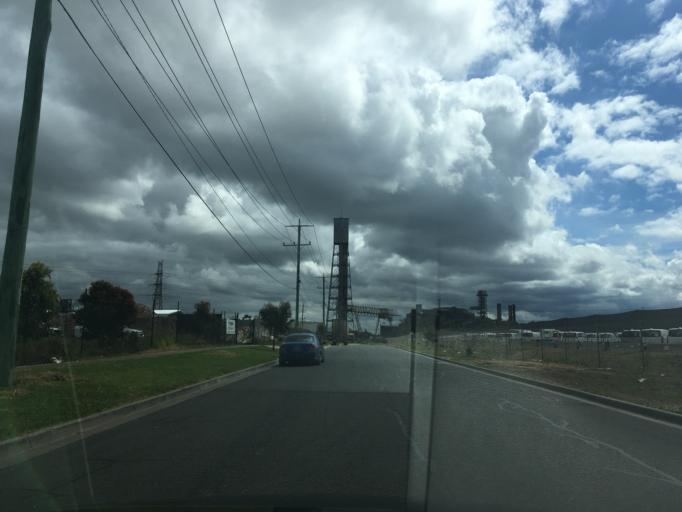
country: AU
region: Victoria
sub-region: Hobsons Bay
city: Laverton
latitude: -37.8379
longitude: 144.7914
